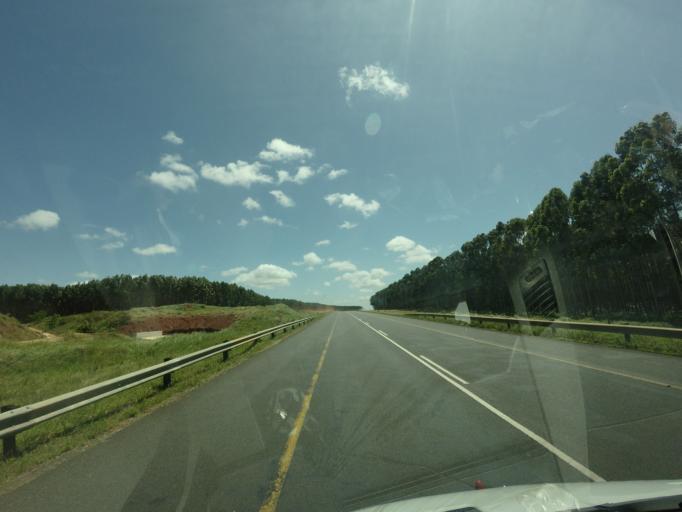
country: ZA
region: KwaZulu-Natal
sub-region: uThungulu District Municipality
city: Empangeni
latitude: -28.7403
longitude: 31.9391
